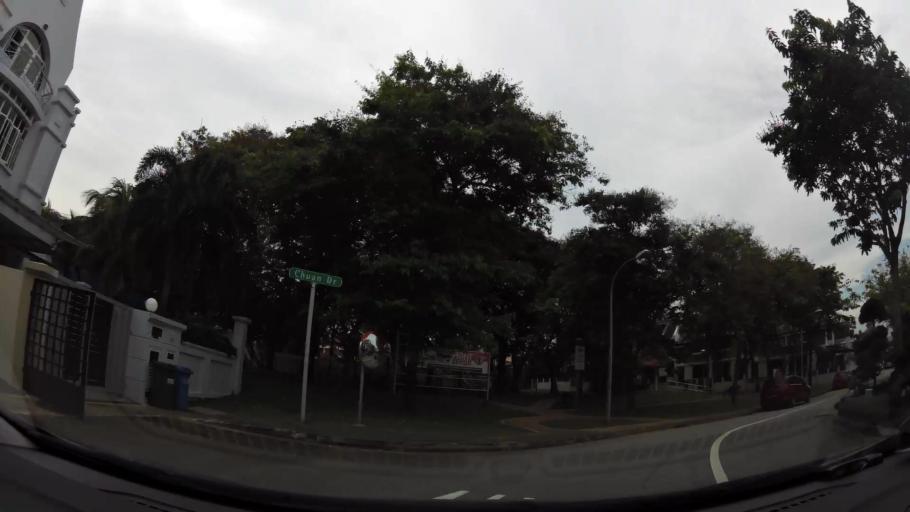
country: SG
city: Singapore
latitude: 1.3603
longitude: 103.8664
